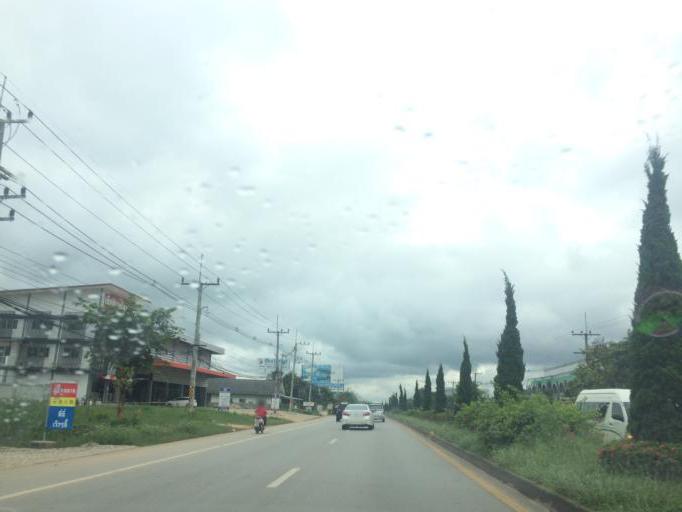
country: TH
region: Chiang Rai
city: Chiang Rai
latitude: 20.0098
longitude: 99.8683
